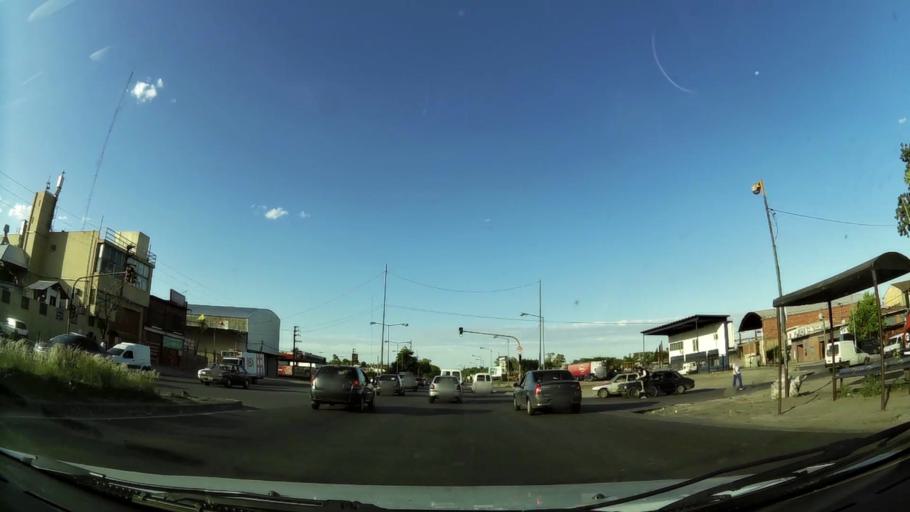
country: AR
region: Buenos Aires
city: Caseros
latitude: -34.5553
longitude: -58.5854
